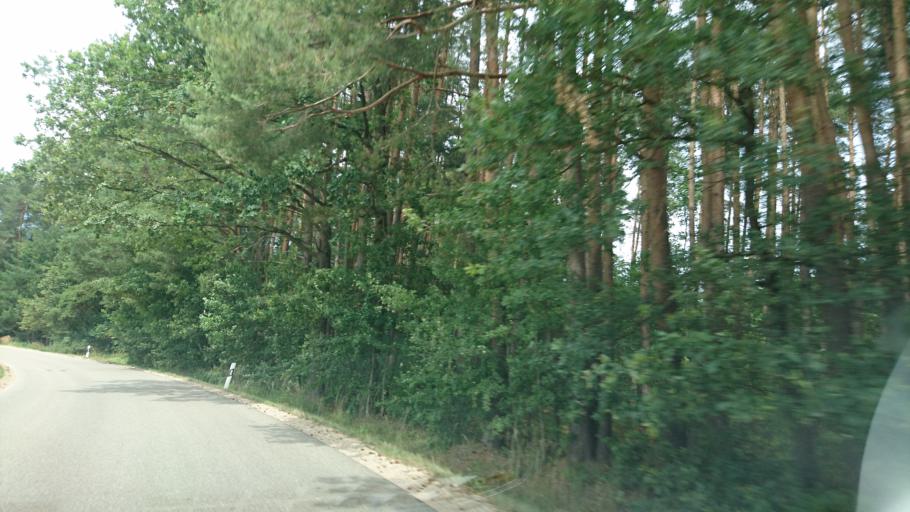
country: DE
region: Bavaria
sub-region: Regierungsbezirk Mittelfranken
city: Roth
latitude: 49.1971
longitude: 11.0986
